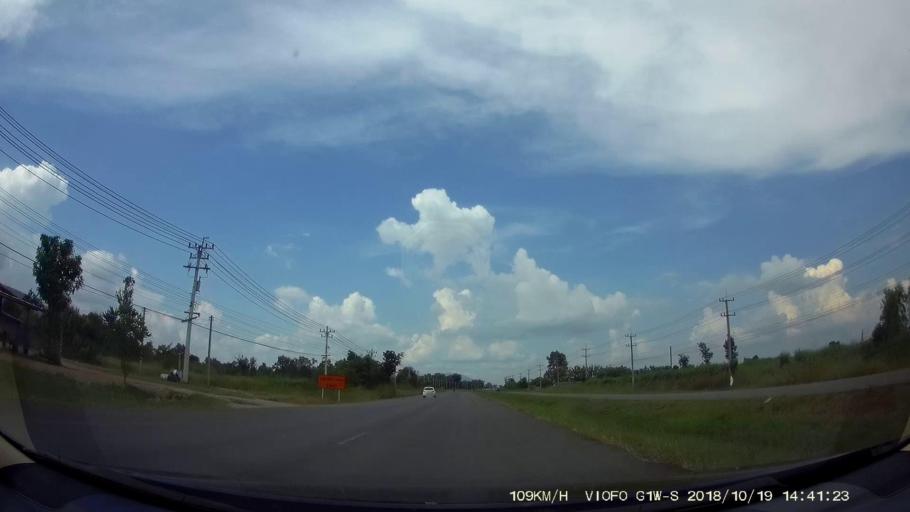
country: TH
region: Chaiyaphum
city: Phu Khiao
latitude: 16.2560
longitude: 102.1989
